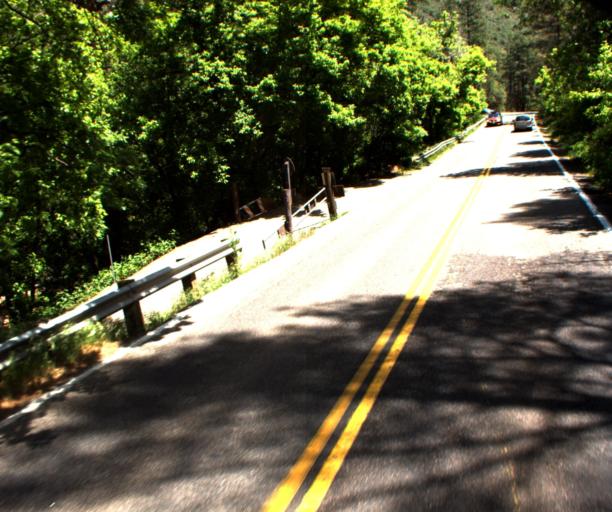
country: US
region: Arizona
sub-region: Coconino County
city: Sedona
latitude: 34.9355
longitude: -111.7448
